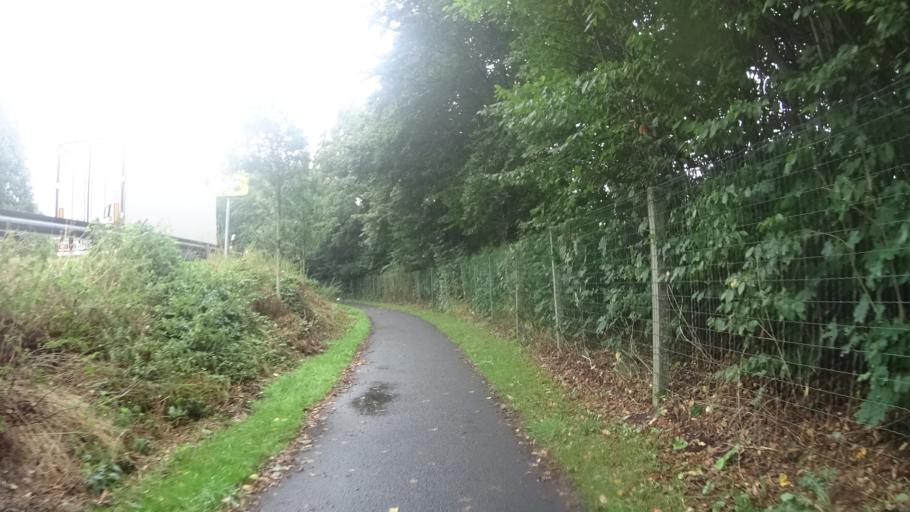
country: DE
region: Lower Saxony
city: Leer
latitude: 53.2390
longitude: 7.4609
